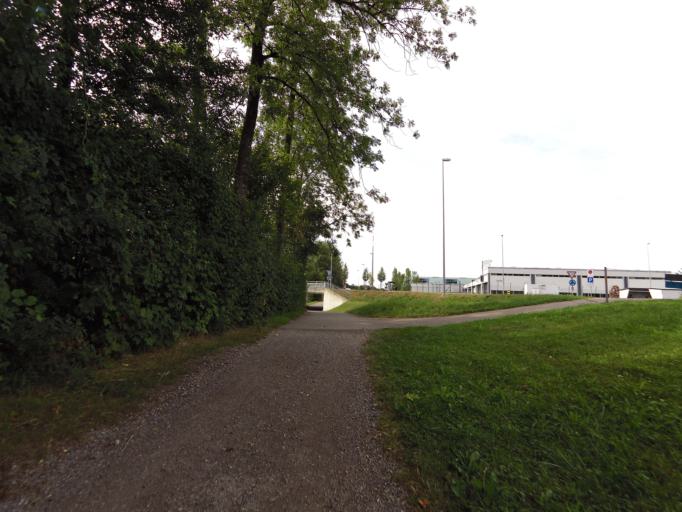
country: CH
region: Zurich
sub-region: Bezirk Buelach
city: Glattbrugg / Rohr/Platten-Balsberg
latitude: 47.4437
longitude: 8.5507
